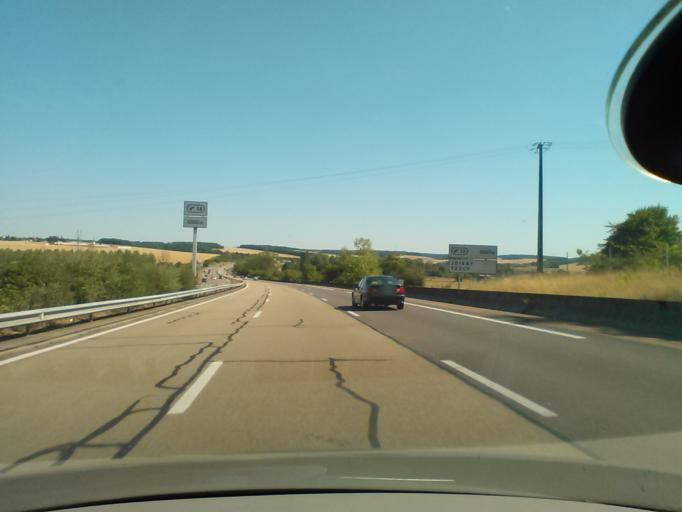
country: FR
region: Bourgogne
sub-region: Departement de l'Yonne
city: Saint-Julien-du-Sault
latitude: 47.9512
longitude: 3.2294
